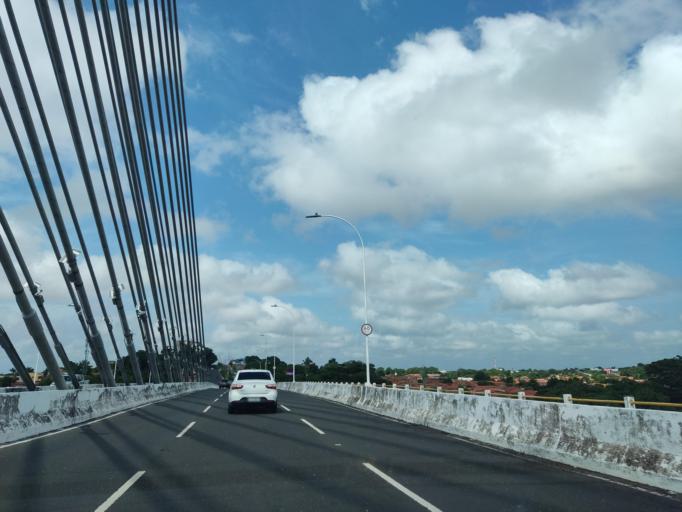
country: BR
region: Piaui
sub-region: Teresina
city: Teresina
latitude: -5.0701
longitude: -42.8030
